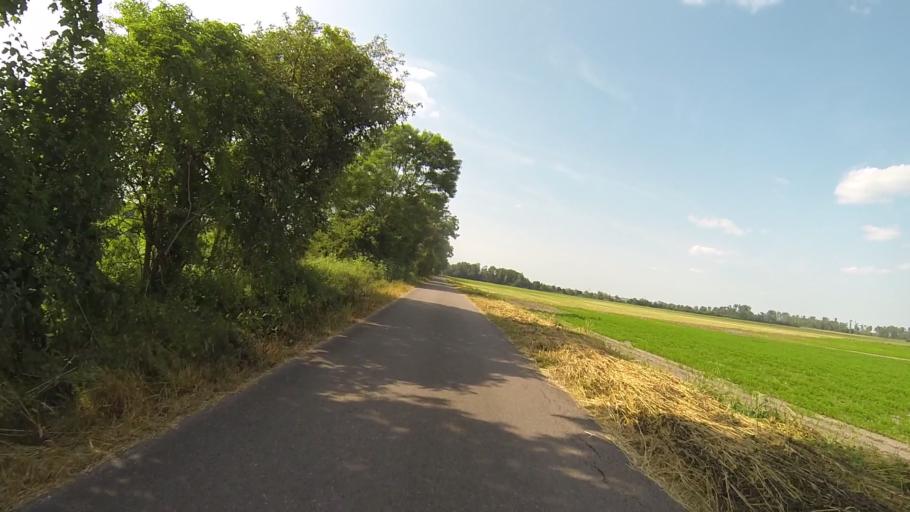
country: DE
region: Baden-Wuerttemberg
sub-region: Tuebingen Region
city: Rammingen
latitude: 48.4842
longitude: 10.1862
